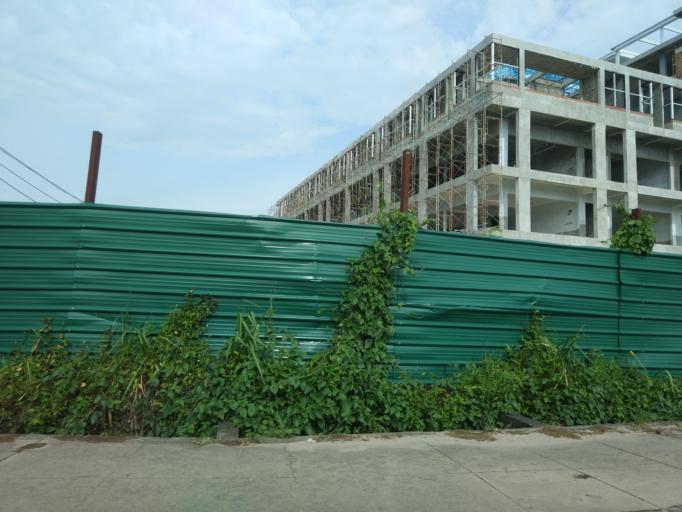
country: MY
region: Sabah
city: Beaufort
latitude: 5.0736
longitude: 115.5490
